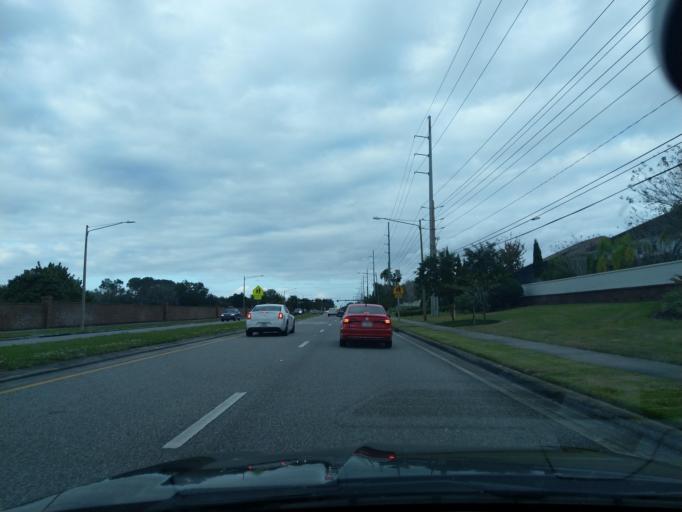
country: US
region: Florida
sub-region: Orange County
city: Doctor Phillips
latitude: 28.4121
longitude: -81.5031
